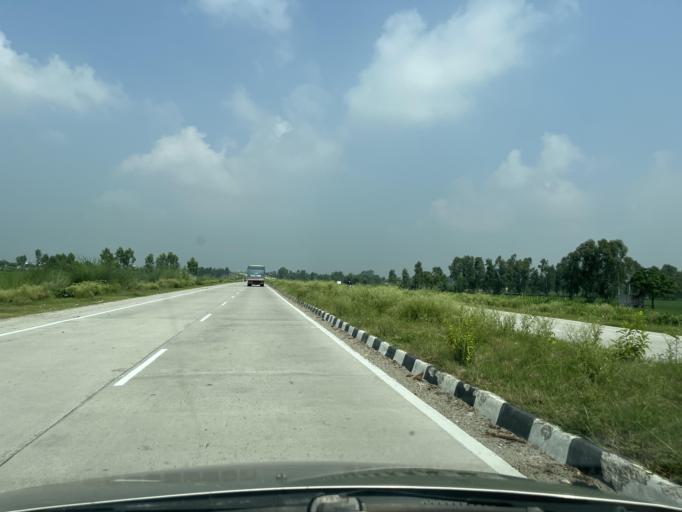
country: IN
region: Uttarakhand
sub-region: Udham Singh Nagar
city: Kashipur
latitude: 29.1676
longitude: 78.9561
